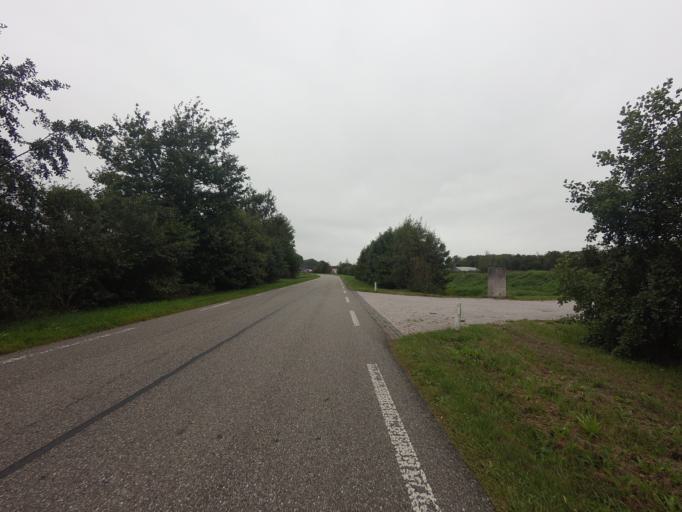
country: NL
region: Friesland
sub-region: Gemeente Opsterland
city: Tijnje
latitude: 53.0255
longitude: 5.9993
